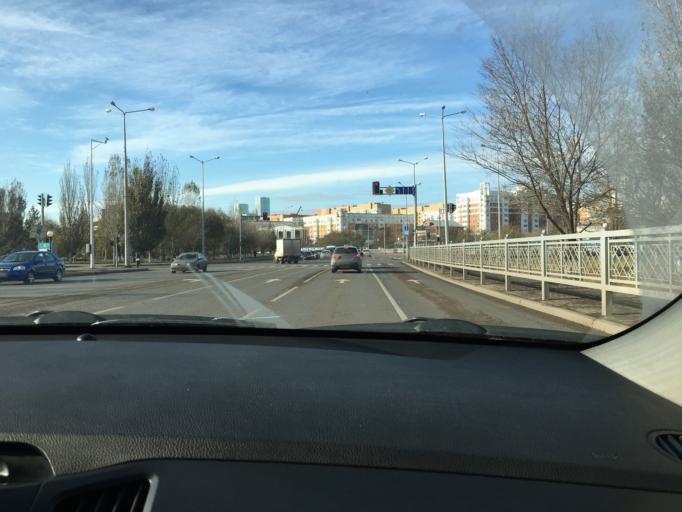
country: KZ
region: Astana Qalasy
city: Astana
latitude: 51.1584
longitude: 71.4430
